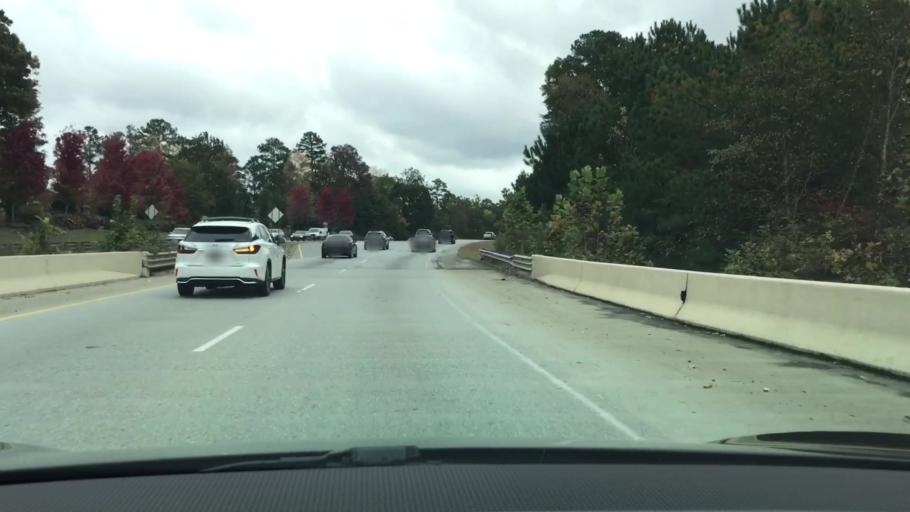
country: US
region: Georgia
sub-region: Gwinnett County
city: Suwanee
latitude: 34.0387
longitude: -84.0744
